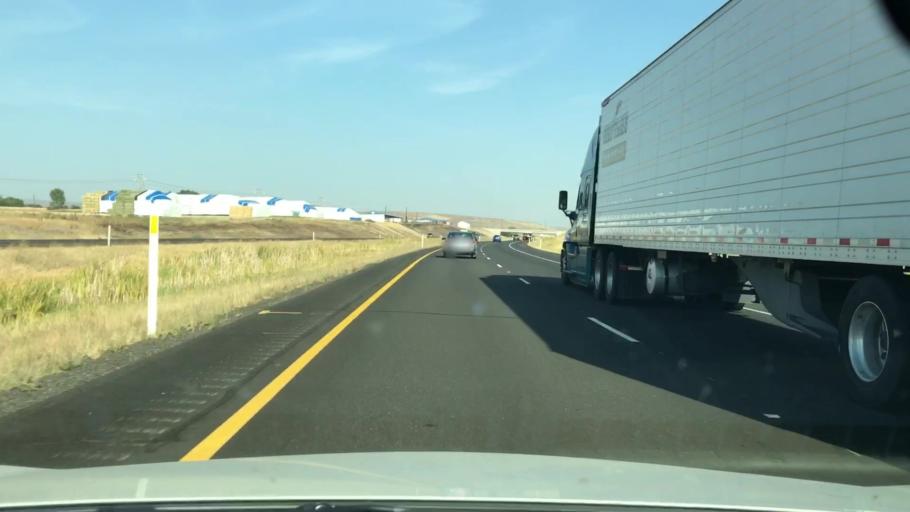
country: US
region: Washington
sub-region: Kittitas County
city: Kittitas
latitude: 46.9728
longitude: -120.3769
